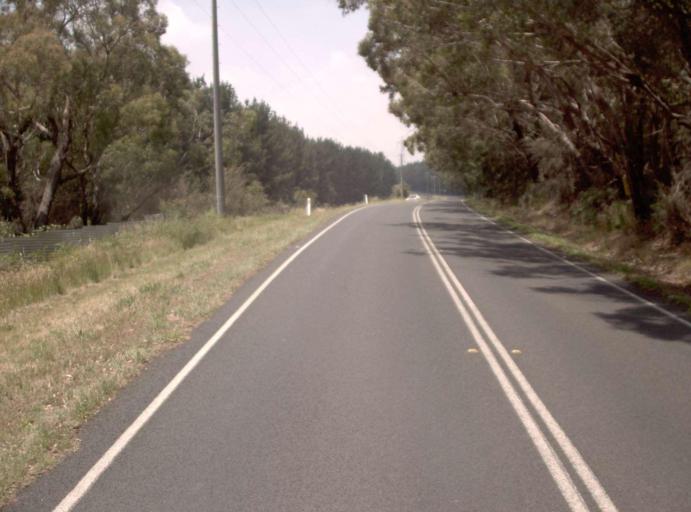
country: AU
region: Victoria
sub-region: Latrobe
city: Traralgon
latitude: -38.2571
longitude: 146.6774
